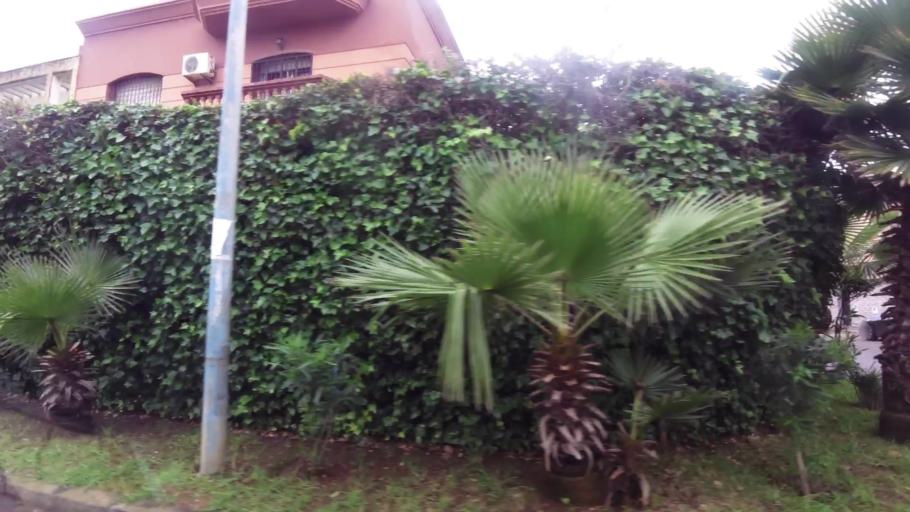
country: MA
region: Grand Casablanca
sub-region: Nouaceur
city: Bouskoura
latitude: 33.5178
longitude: -7.6443
